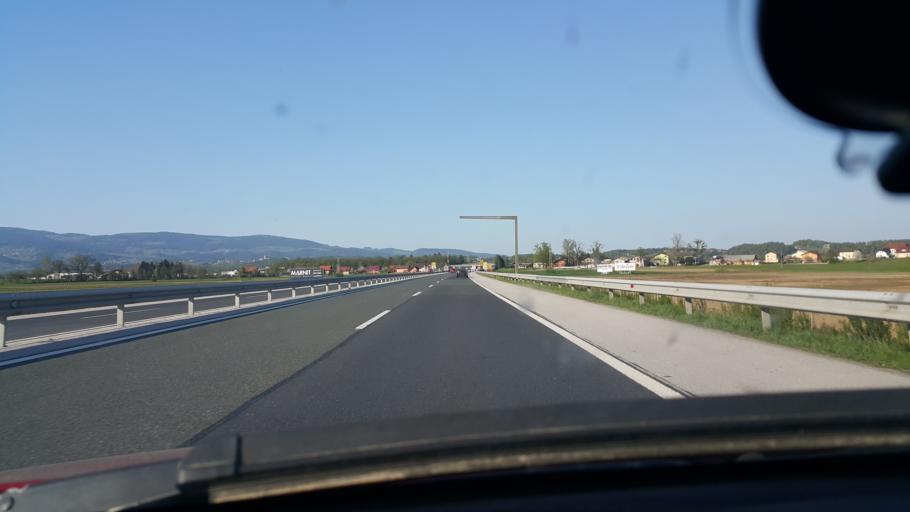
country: SI
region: Slovenska Konjice
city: Slovenske Konjice
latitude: 46.3320
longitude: 15.4698
